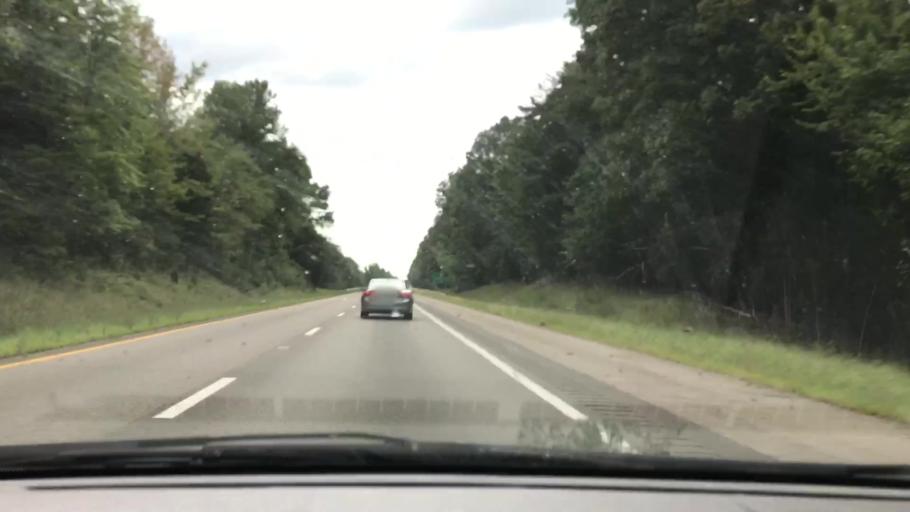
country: US
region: Virginia
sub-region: Goochland County
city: Goochland
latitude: 37.8388
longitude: -77.9755
